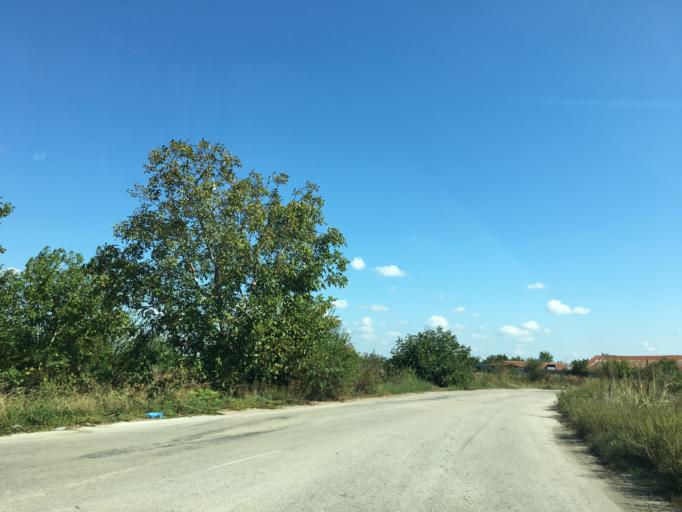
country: RO
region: Dolj
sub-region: Comuna Desa
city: Desa
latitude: 43.7727
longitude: 22.9925
